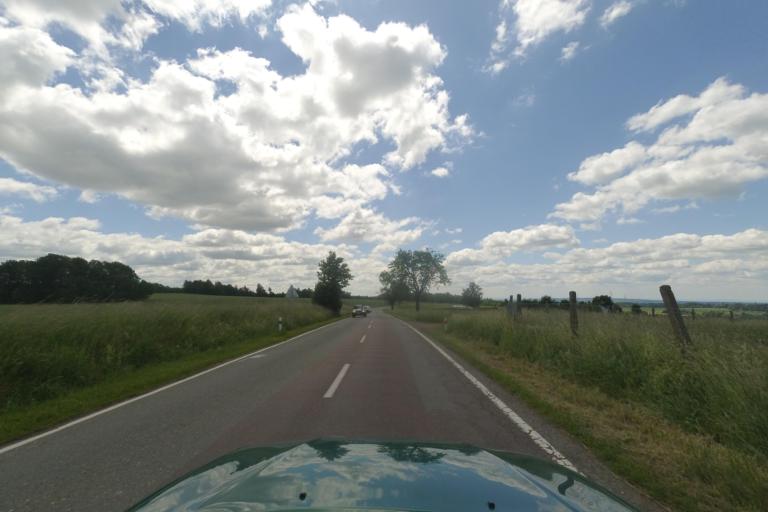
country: CZ
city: Nove Mesto nad Metuji
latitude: 50.3367
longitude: 16.2229
